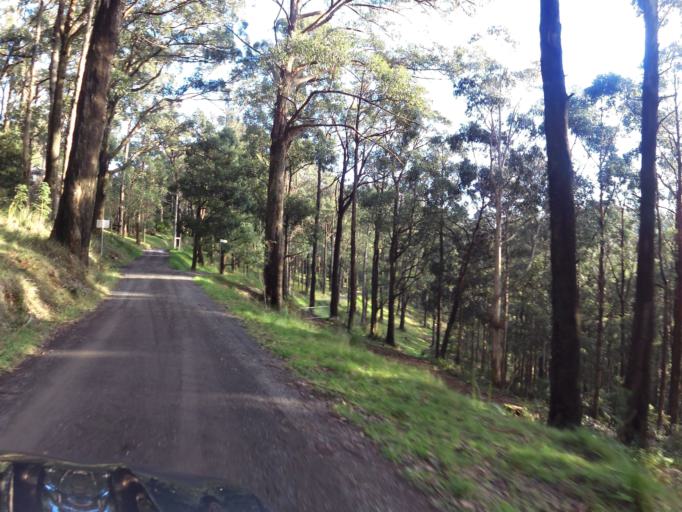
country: AU
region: Victoria
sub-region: Yarra Ranges
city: Ferny Creek
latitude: -37.8759
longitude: 145.3334
